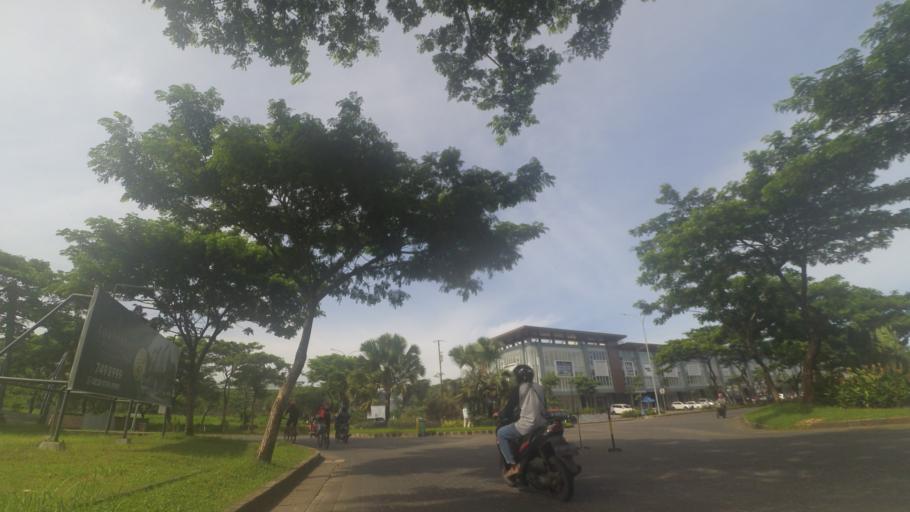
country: ID
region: West Java
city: Pamulang
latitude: -6.3445
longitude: 106.7678
